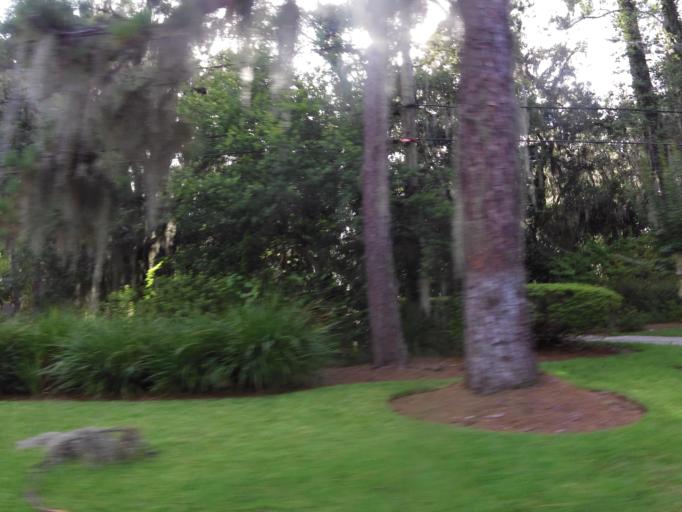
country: US
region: Florida
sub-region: Duval County
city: Jacksonville
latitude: 30.2656
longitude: -81.7158
